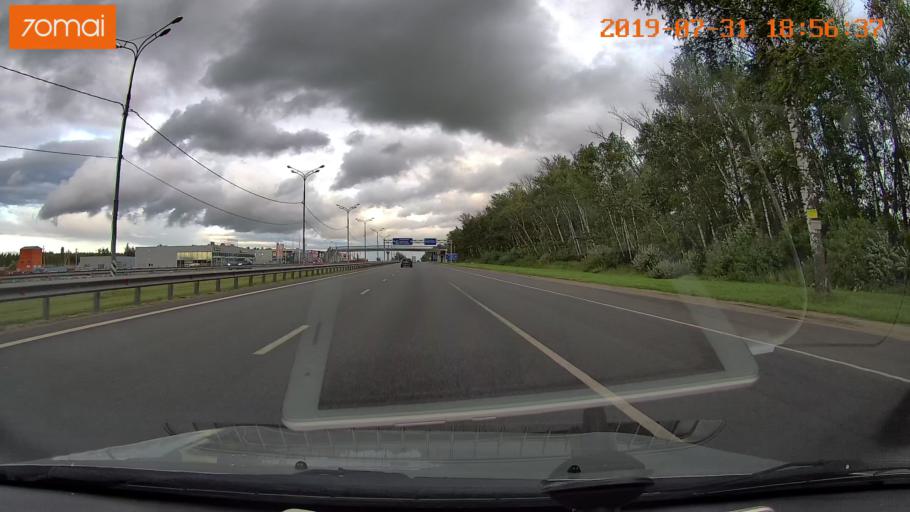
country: RU
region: Moskovskaya
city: Raduzhnyy
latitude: 55.1614
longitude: 38.6805
